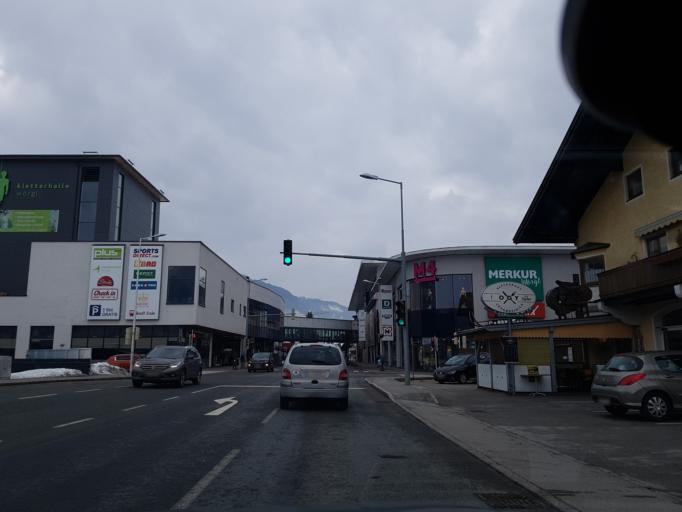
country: AT
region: Tyrol
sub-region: Politischer Bezirk Kufstein
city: Worgl
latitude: 47.4892
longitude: 12.0716
